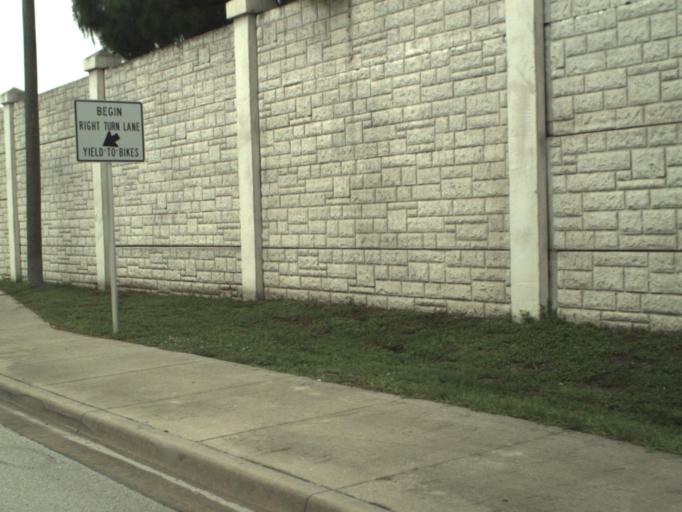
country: US
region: Florida
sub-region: Palm Beach County
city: Schall Circle
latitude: 26.7420
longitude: -80.1098
